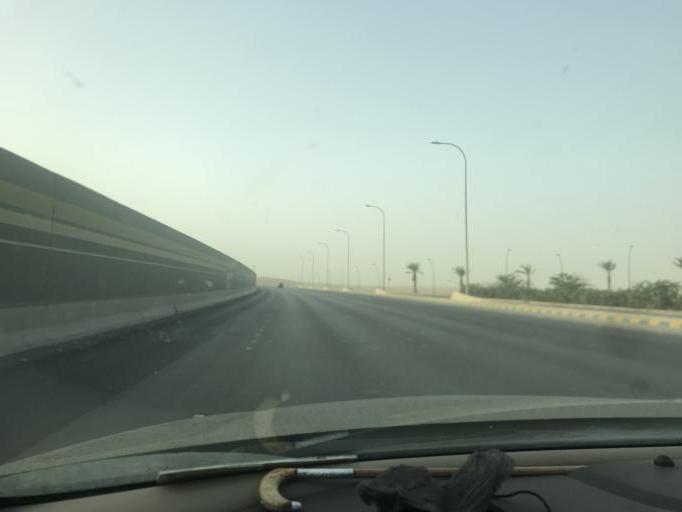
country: SA
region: Ar Riyad
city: Riyadh
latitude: 24.8894
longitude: 46.6948
